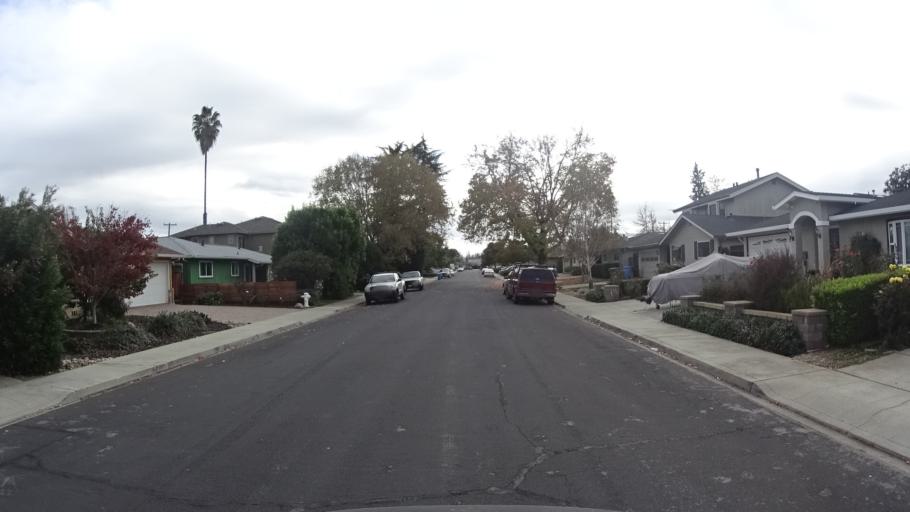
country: US
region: California
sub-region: Santa Clara County
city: Cupertino
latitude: 37.3266
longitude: -121.9897
